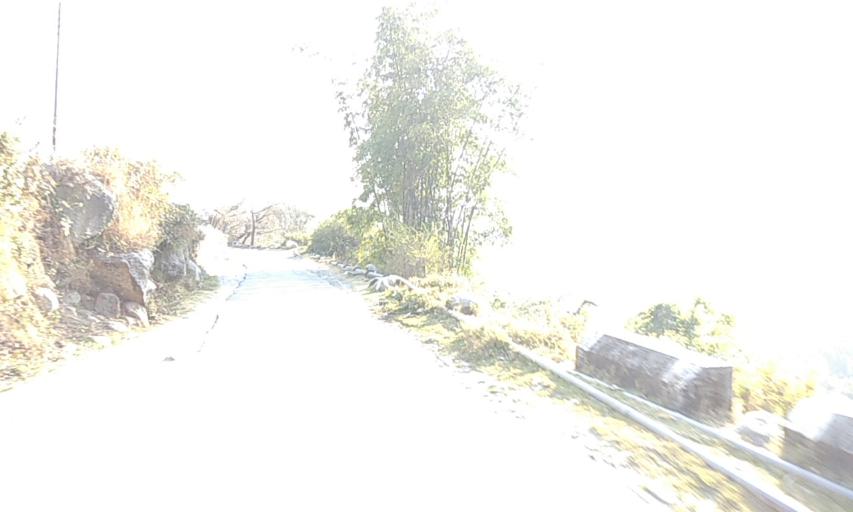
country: IN
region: Himachal Pradesh
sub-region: Kangra
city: Palampur
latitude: 32.1319
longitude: 76.5360
